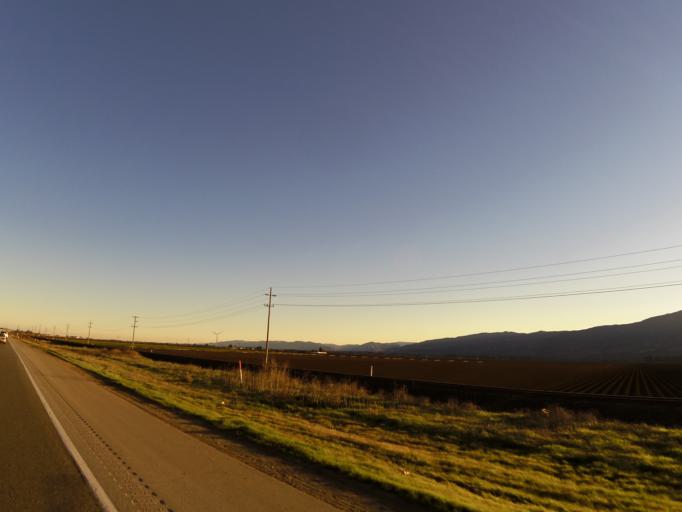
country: US
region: California
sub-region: Monterey County
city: Soledad
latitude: 36.4439
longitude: -121.3562
